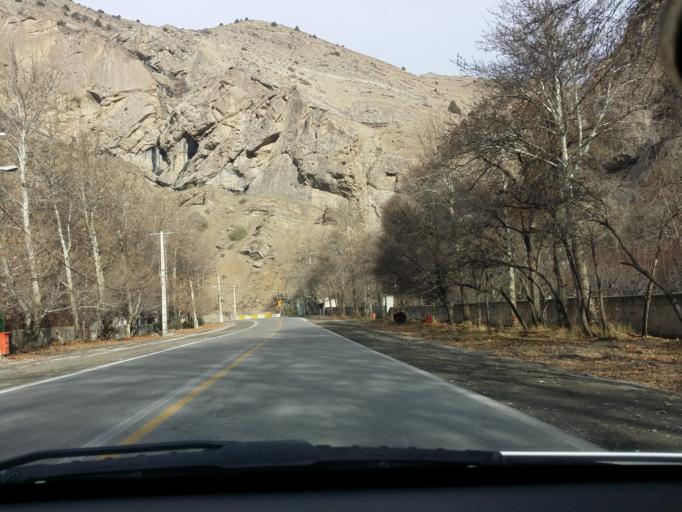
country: IR
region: Tehran
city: Tajrish
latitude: 36.0310
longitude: 51.2225
